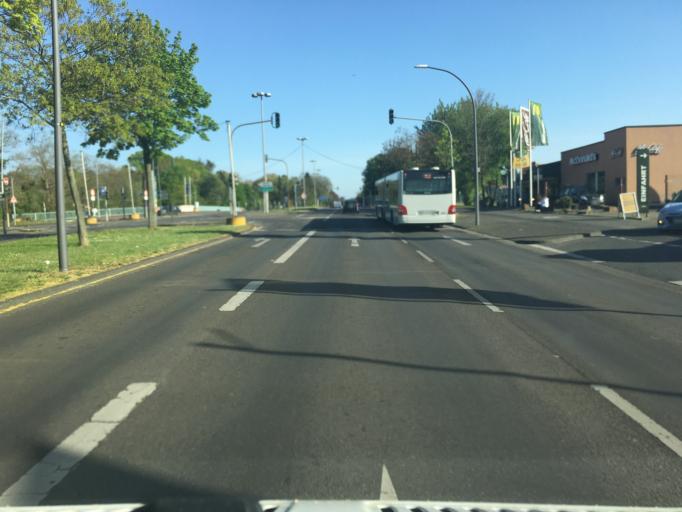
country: DE
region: North Rhine-Westphalia
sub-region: Regierungsbezirk Koln
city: Buchheim
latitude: 50.9496
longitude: 7.0184
